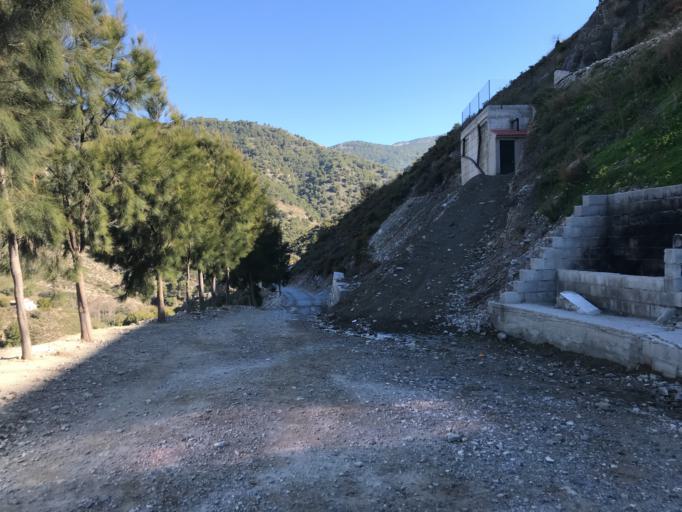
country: ES
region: Andalusia
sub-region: Provincia de Malaga
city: Canillas de Albaida
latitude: 36.8477
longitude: -3.9879
